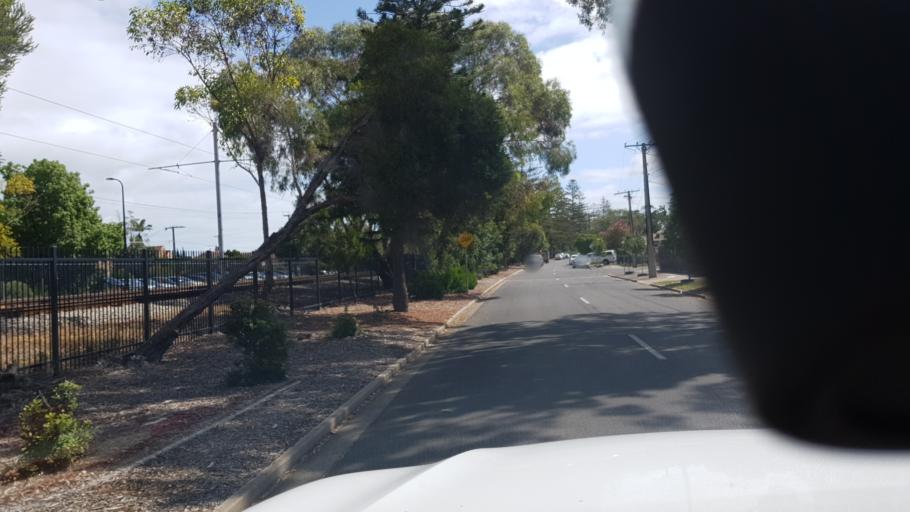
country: AU
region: South Australia
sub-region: Holdfast Bay
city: Glenelg East
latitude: -34.9780
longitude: 138.5333
